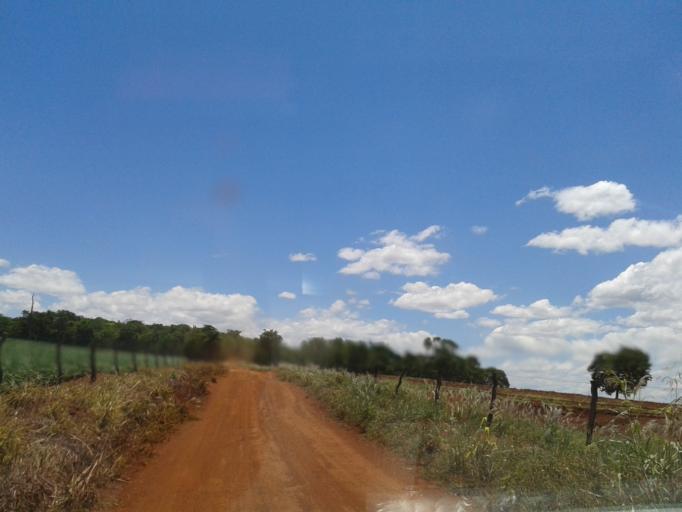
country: BR
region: Minas Gerais
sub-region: Centralina
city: Centralina
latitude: -18.6813
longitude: -49.2262
